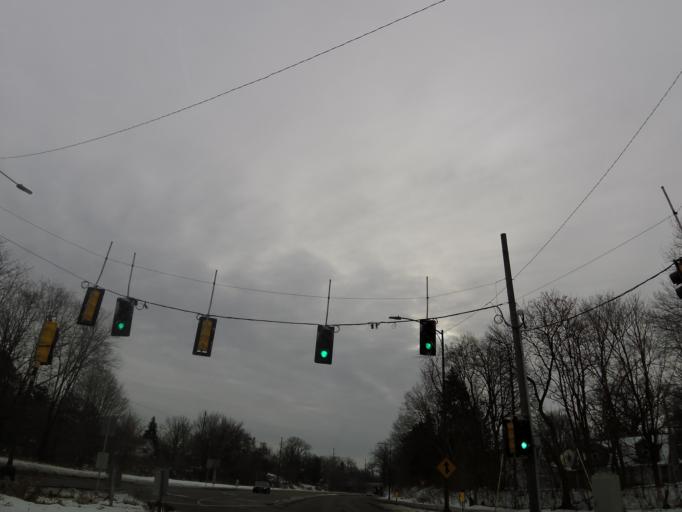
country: US
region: Minnesota
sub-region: Ramsey County
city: Falcon Heights
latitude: 44.9440
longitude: -93.1553
